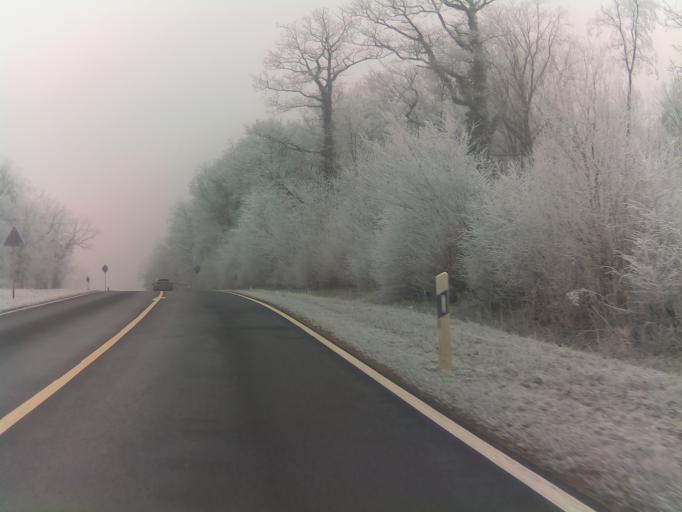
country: DE
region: Bavaria
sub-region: Regierungsbezirk Unterfranken
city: Wonfurt
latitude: 50.0195
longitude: 10.4892
